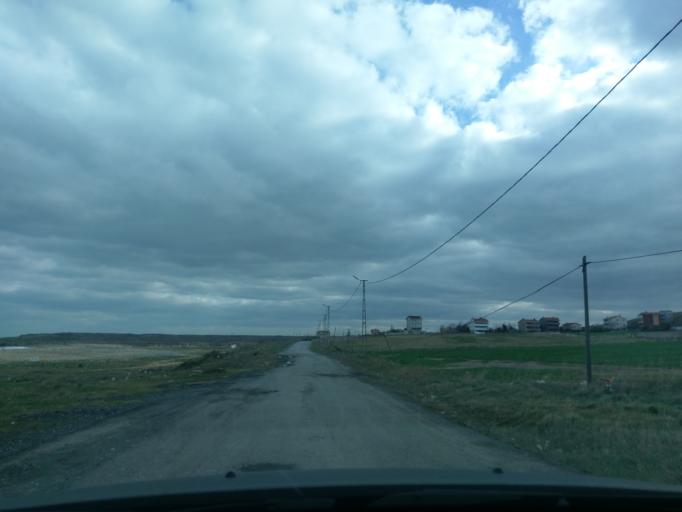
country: TR
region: Istanbul
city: Durusu
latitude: 41.3258
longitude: 28.7246
